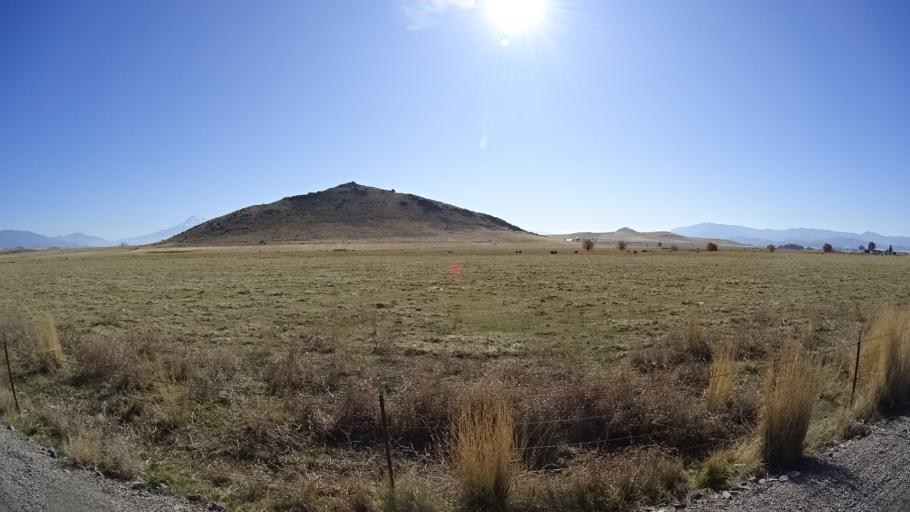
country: US
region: California
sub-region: Siskiyou County
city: Montague
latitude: 41.7565
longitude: -122.4900
